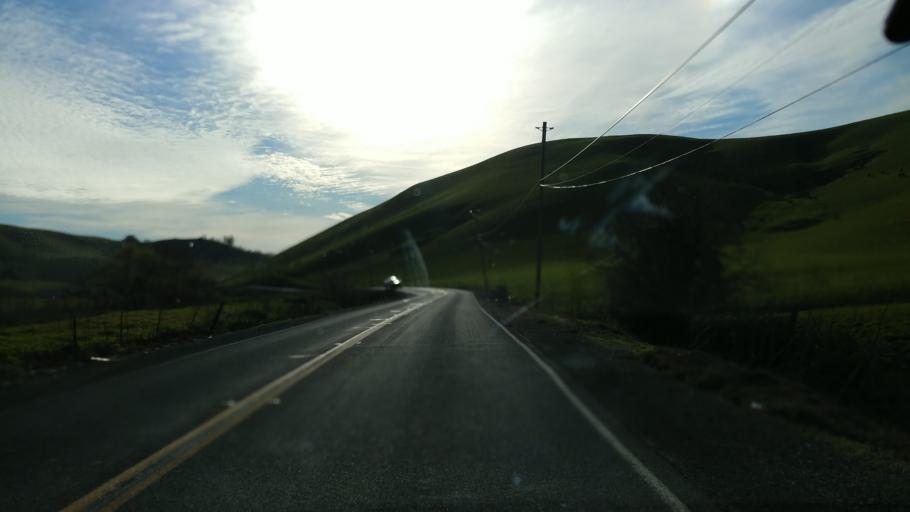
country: US
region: California
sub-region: Contra Costa County
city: Blackhawk
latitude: 37.7787
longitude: -121.8438
